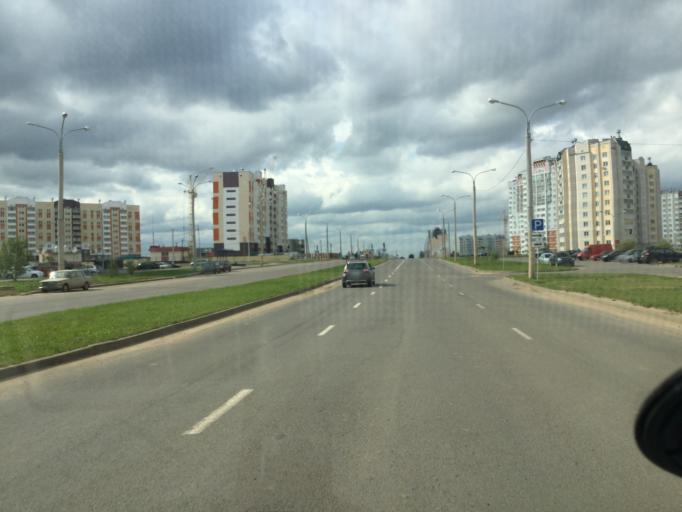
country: BY
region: Vitebsk
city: Vitebsk
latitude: 55.1642
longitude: 30.2731
